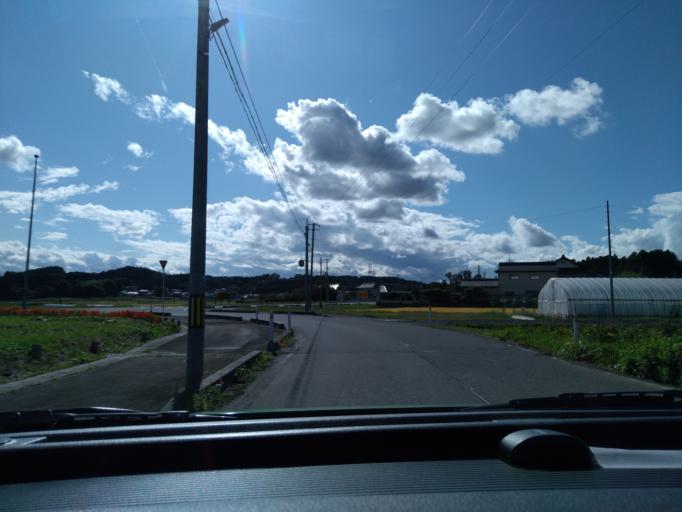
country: JP
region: Iwate
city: Ichinoseki
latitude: 38.7688
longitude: 141.1835
